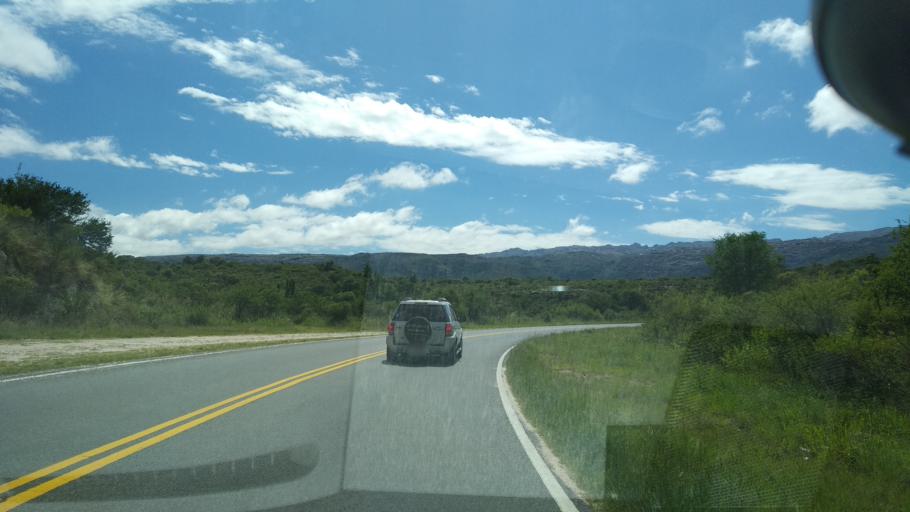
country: AR
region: Cordoba
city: Mina Clavero
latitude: -31.7552
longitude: -64.9587
